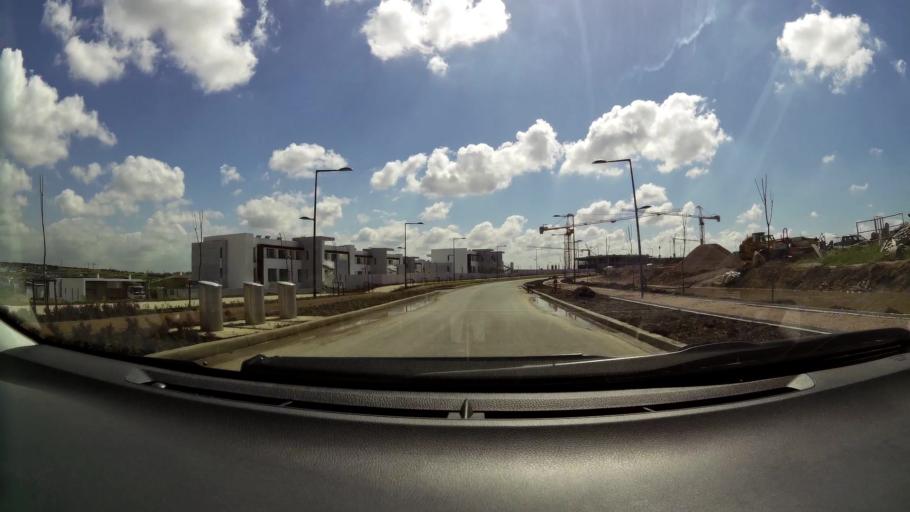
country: MA
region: Grand Casablanca
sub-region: Nouaceur
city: Bouskoura
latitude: 33.4906
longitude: -7.6037
